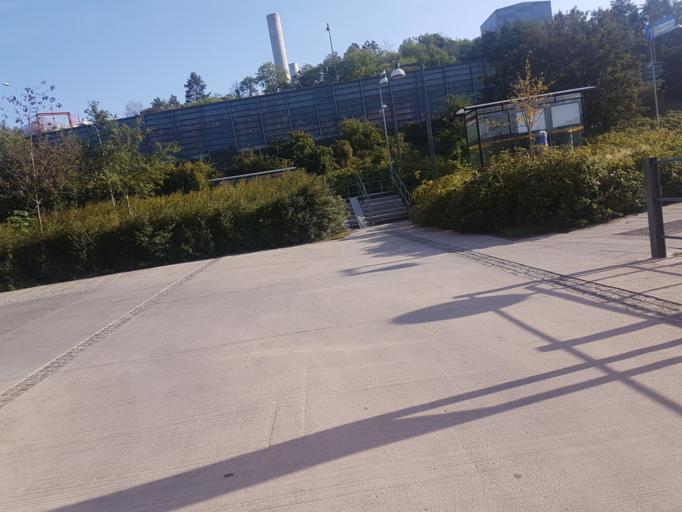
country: SE
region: Stockholm
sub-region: Stockholms Kommun
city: OEstermalm
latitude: 59.3081
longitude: 18.1059
